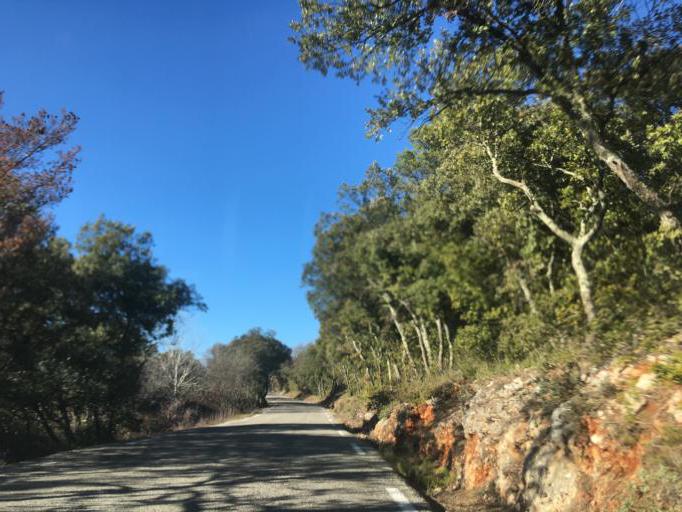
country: FR
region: Provence-Alpes-Cote d'Azur
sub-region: Departement du Var
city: Barjols
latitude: 43.5922
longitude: 6.0677
